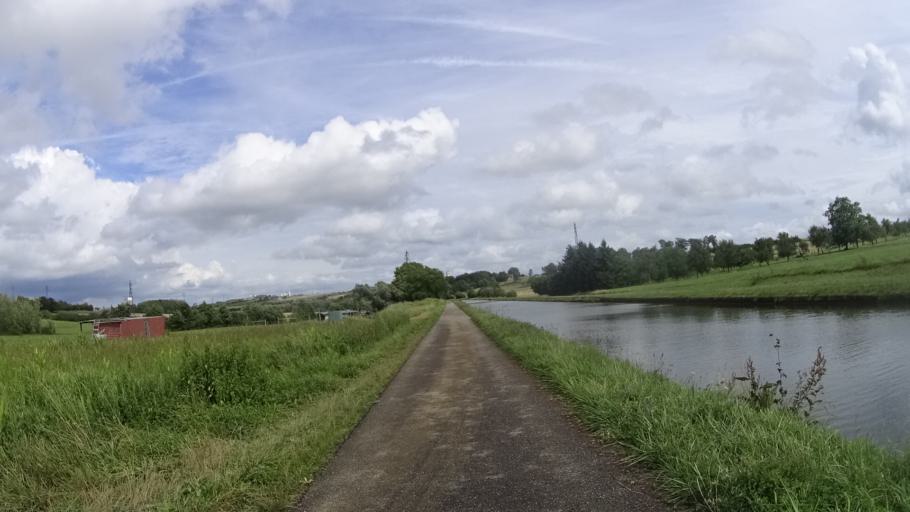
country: FR
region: Lorraine
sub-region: Departement de la Moselle
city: Lorquin
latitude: 48.6817
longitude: 6.9387
